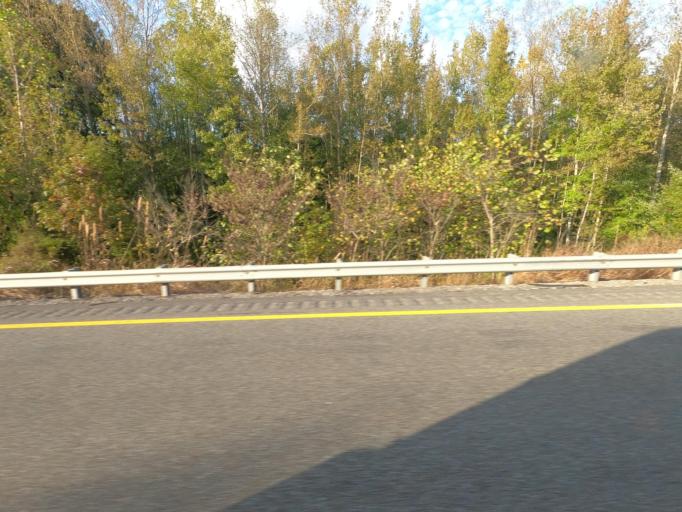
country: US
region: Tennessee
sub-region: Decatur County
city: Parsons
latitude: 35.8145
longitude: -88.2151
